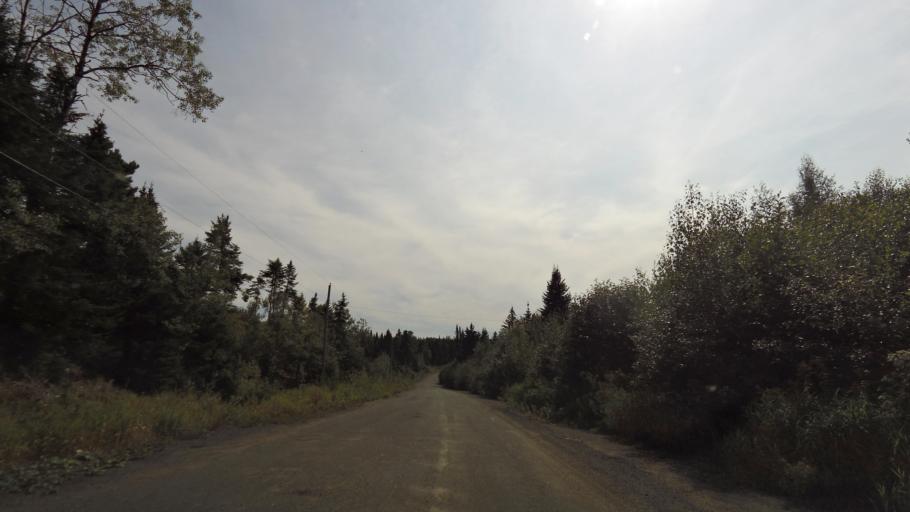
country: CA
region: New Brunswick
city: Hampton
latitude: 45.5796
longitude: -65.8306
